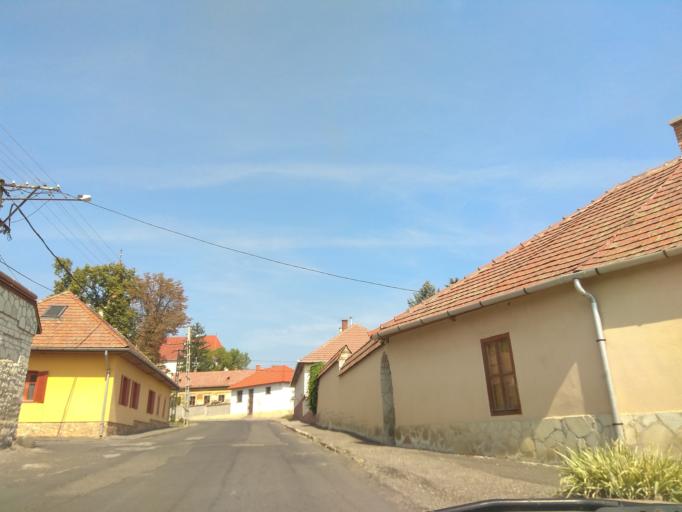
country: HU
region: Borsod-Abauj-Zemplen
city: Tallya
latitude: 48.2328
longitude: 21.2349
